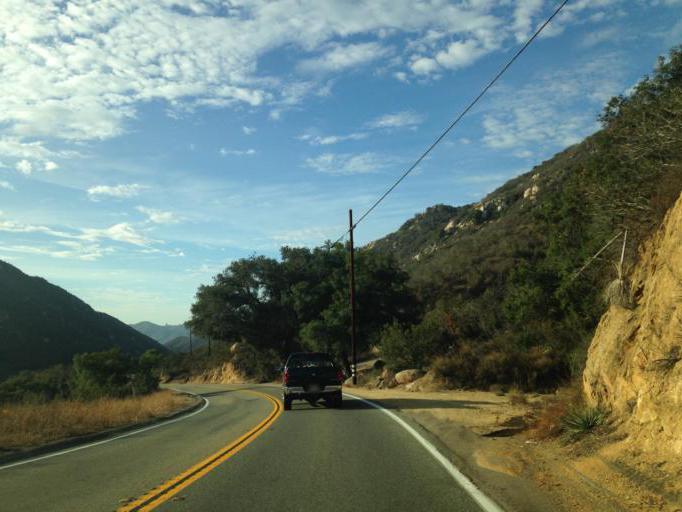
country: US
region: California
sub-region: San Diego County
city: Rainbow
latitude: 33.4007
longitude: -117.0836
